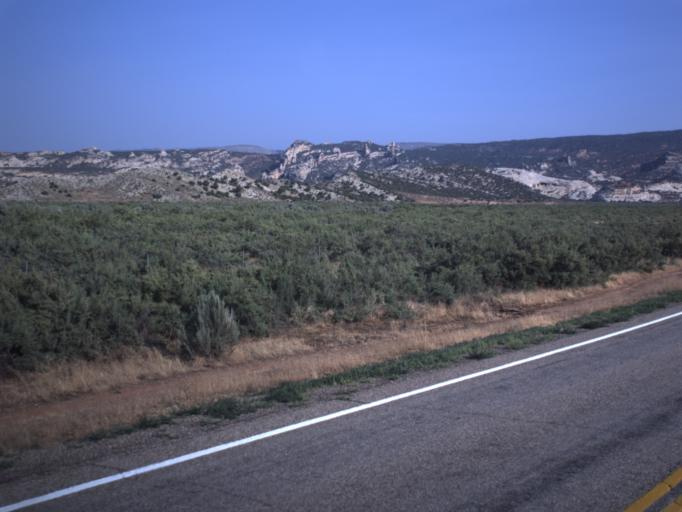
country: US
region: Utah
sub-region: Uintah County
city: Vernal
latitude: 40.5351
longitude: -109.5225
